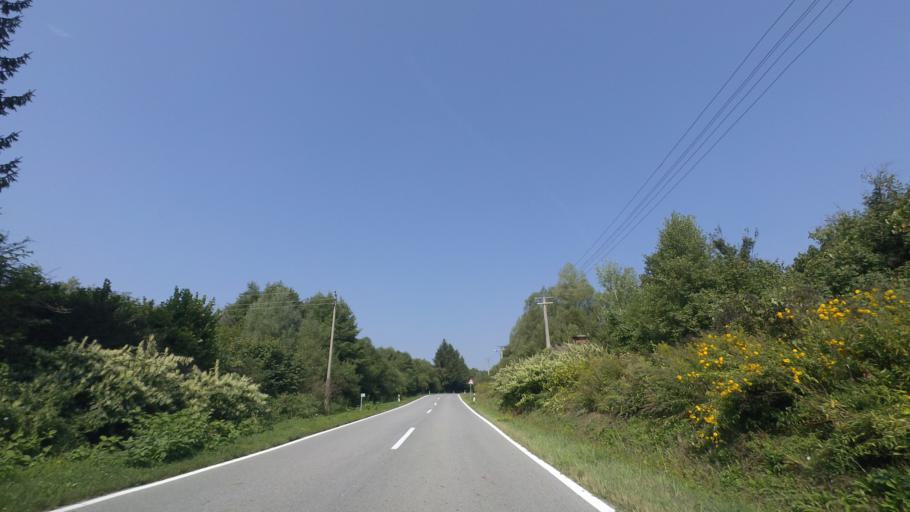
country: HR
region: Brodsko-Posavska
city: Cernik
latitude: 45.4572
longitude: 17.4200
